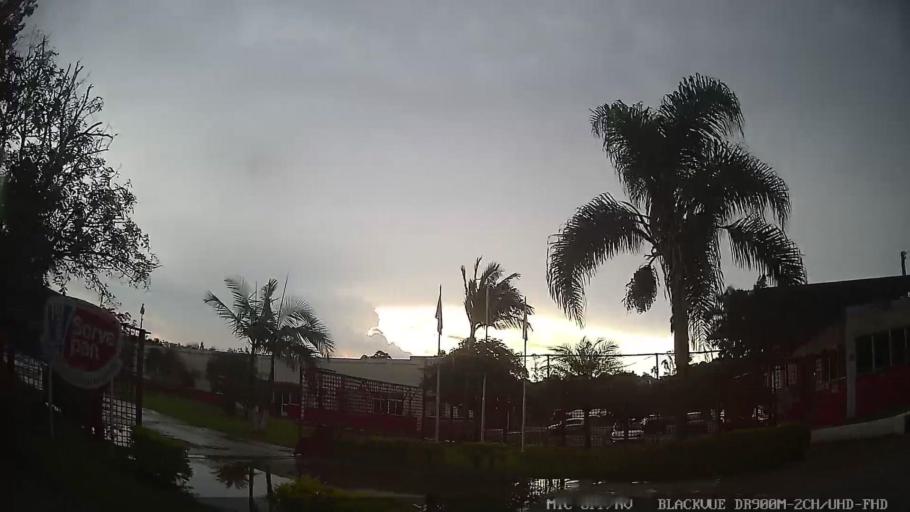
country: BR
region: Sao Paulo
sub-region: Ribeirao Pires
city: Ribeirao Pires
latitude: -23.6862
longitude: -46.3606
